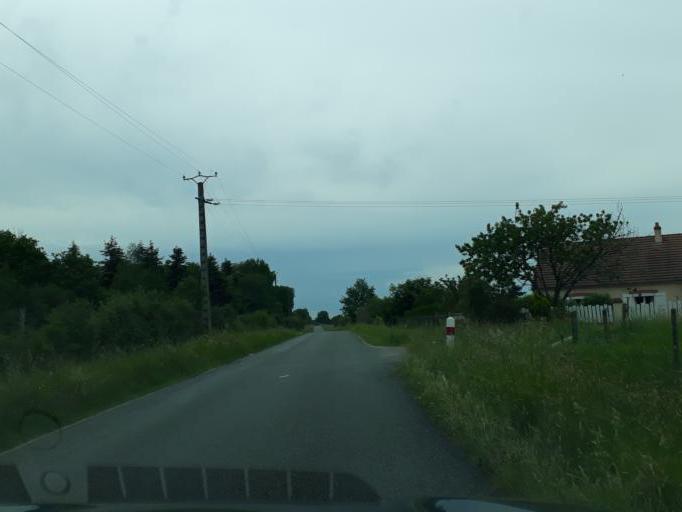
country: FR
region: Centre
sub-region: Departement du Loiret
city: Saint-Benoit-sur-Loire
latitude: 47.7393
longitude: 2.2719
